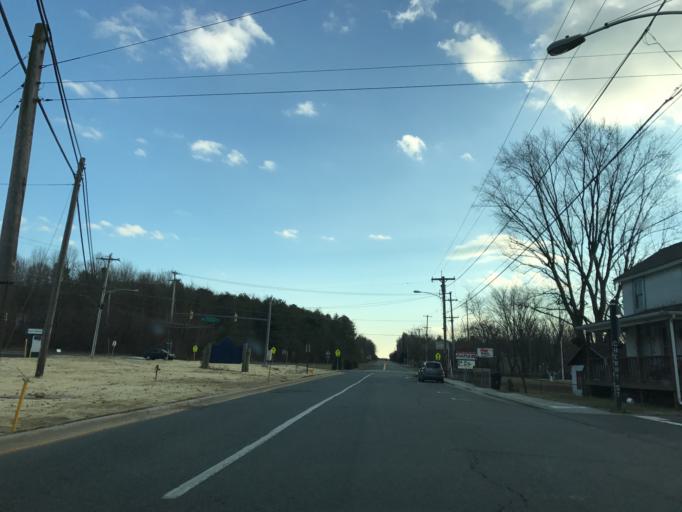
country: US
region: Maryland
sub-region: Cecil County
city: North East
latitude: 39.5931
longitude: -75.9416
